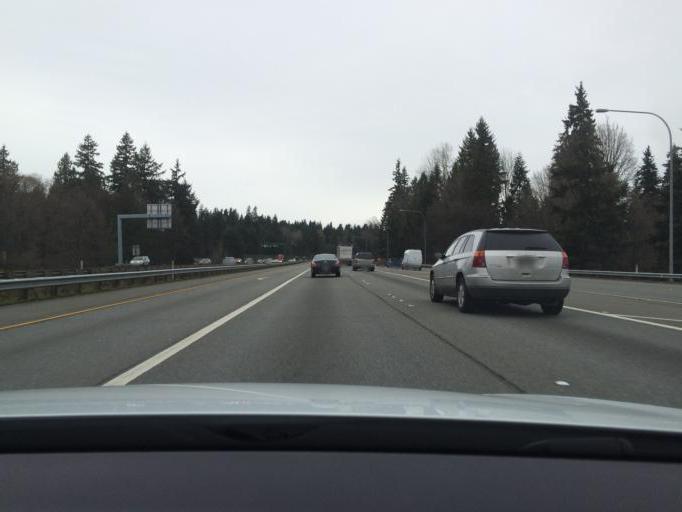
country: US
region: Washington
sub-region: King County
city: Bothell
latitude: 47.7967
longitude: -122.2177
